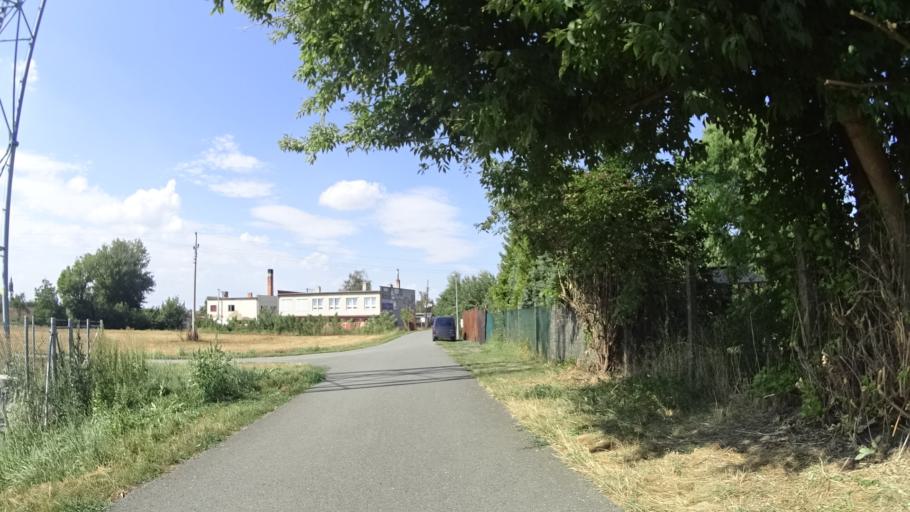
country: CZ
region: Zlin
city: Uhersky Ostroh
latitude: 48.9811
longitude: 17.3965
